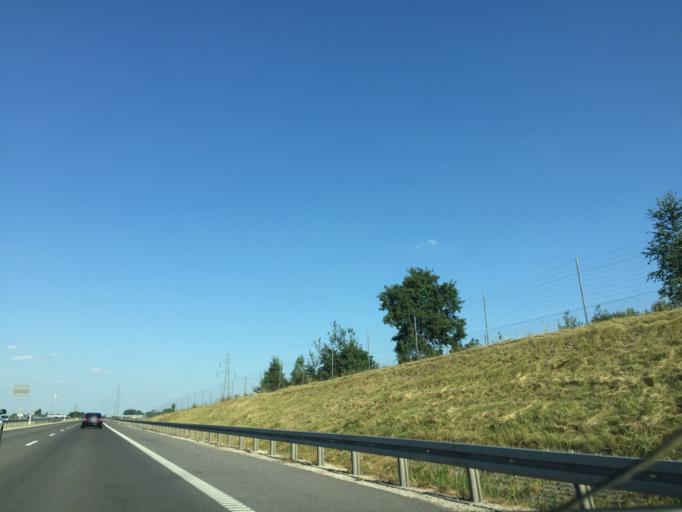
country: PL
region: Swietokrzyskie
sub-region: Powiat jedrzejowski
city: Jedrzejow
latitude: 50.6250
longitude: 20.2994
